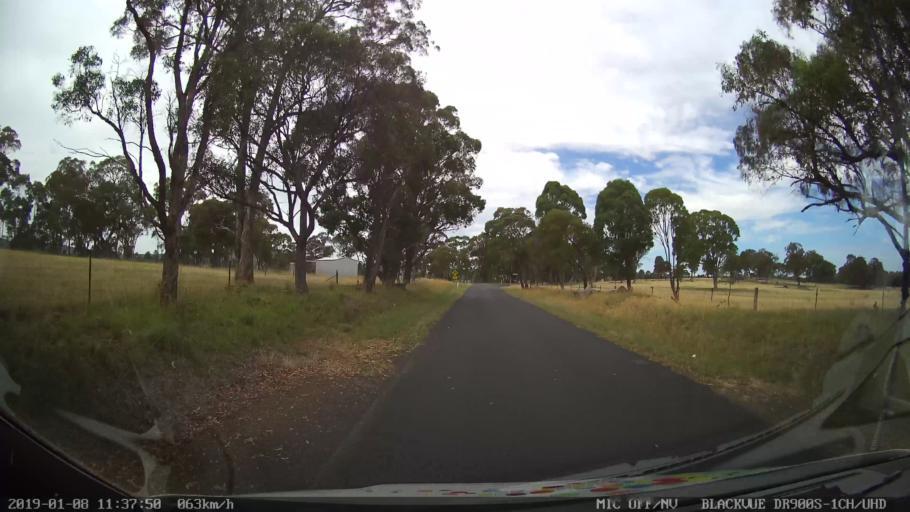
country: AU
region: New South Wales
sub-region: Guyra
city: Guyra
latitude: -30.3552
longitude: 151.5543
